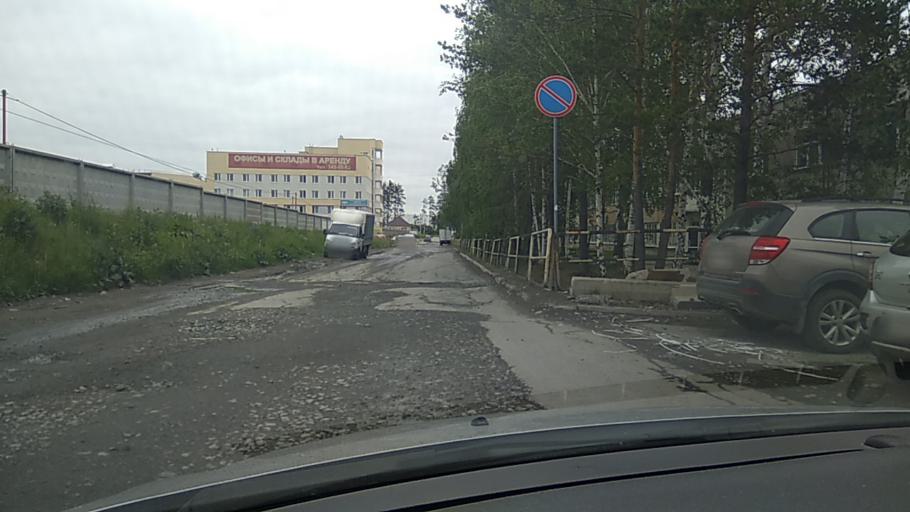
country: RU
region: Sverdlovsk
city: Shuvakish
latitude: 56.8933
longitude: 60.5166
